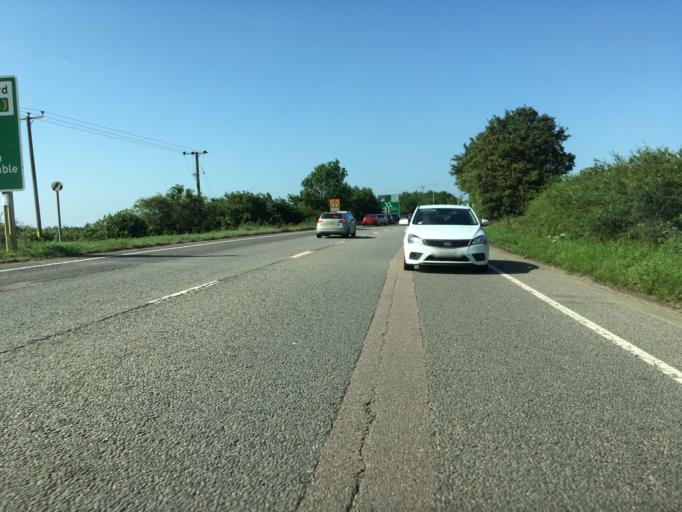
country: GB
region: England
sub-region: Milton Keynes
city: Water Eaton
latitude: 51.9895
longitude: -0.7013
